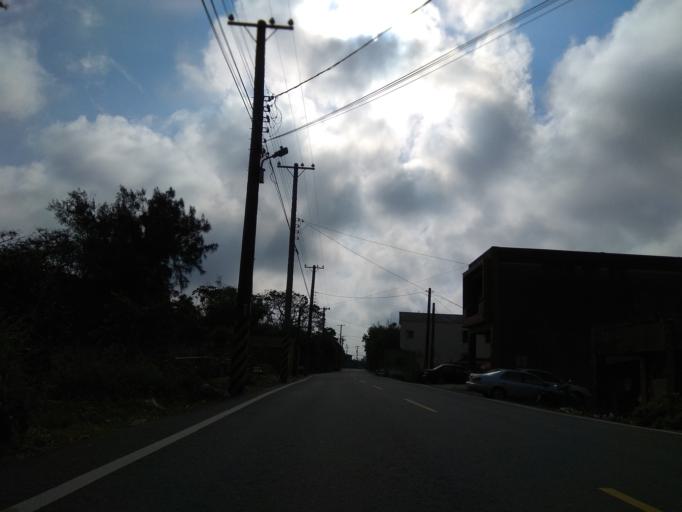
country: TW
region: Taiwan
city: Taoyuan City
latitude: 25.0579
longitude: 121.1512
